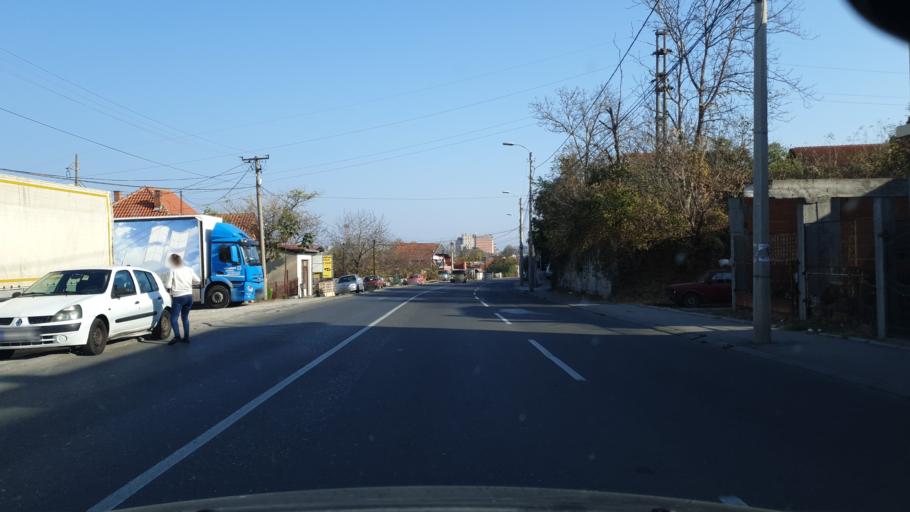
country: RS
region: Central Serbia
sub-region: Nisavski Okrug
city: Nis
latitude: 43.3158
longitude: 21.8601
